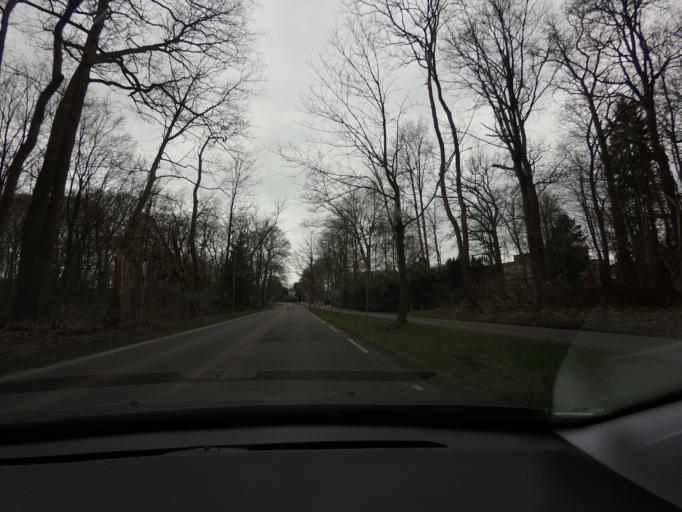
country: NL
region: Utrecht
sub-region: Gemeente Utrechtse Heuvelrug
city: Doorn
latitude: 52.0275
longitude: 5.3511
